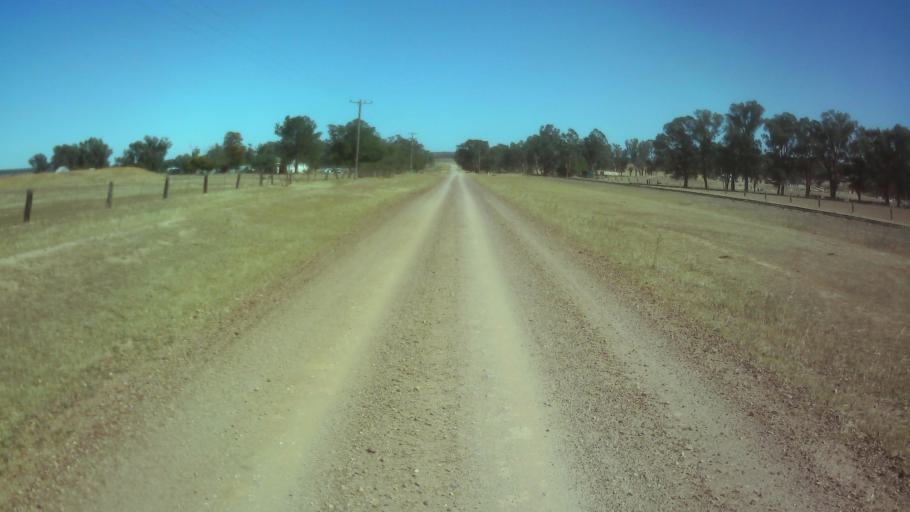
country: AU
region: New South Wales
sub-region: Weddin
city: Grenfell
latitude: -33.9456
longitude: 148.2940
